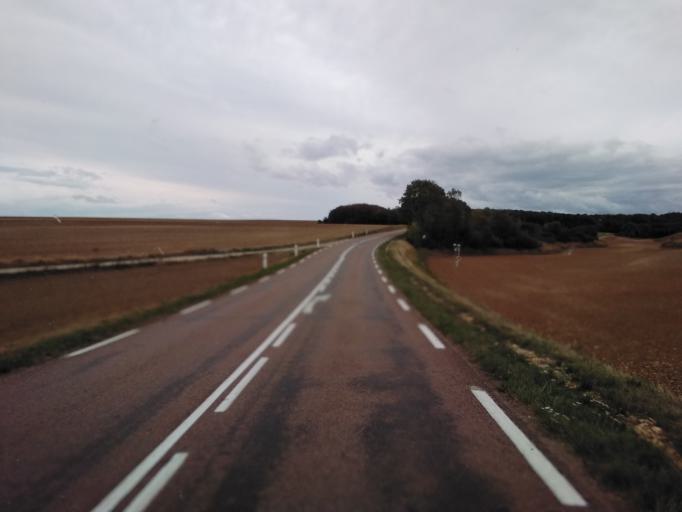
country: FR
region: Champagne-Ardenne
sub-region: Departement de l'Aube
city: Bar-sur-Seine
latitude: 48.1621
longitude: 4.4147
